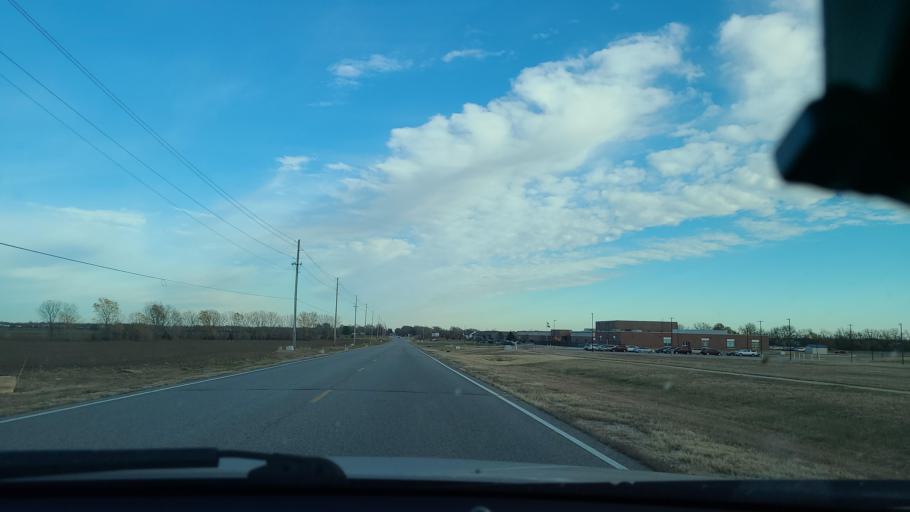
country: US
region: Kansas
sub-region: Sedgwick County
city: Goddard
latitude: 37.6496
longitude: -97.5665
